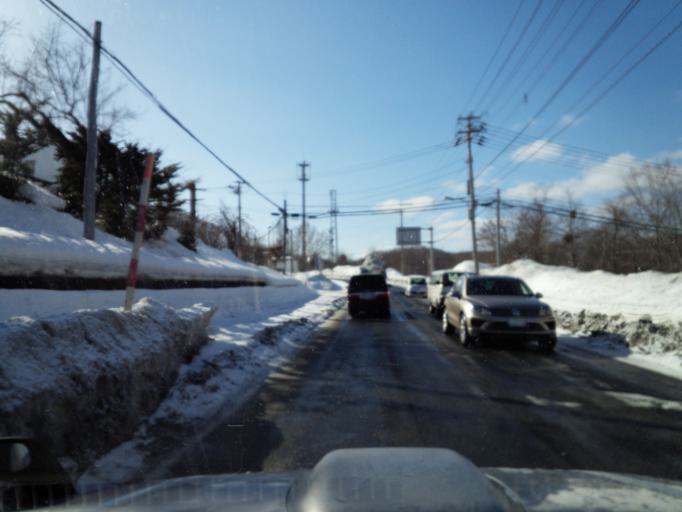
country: JP
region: Hokkaido
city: Sapporo
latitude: 42.9346
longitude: 141.3417
